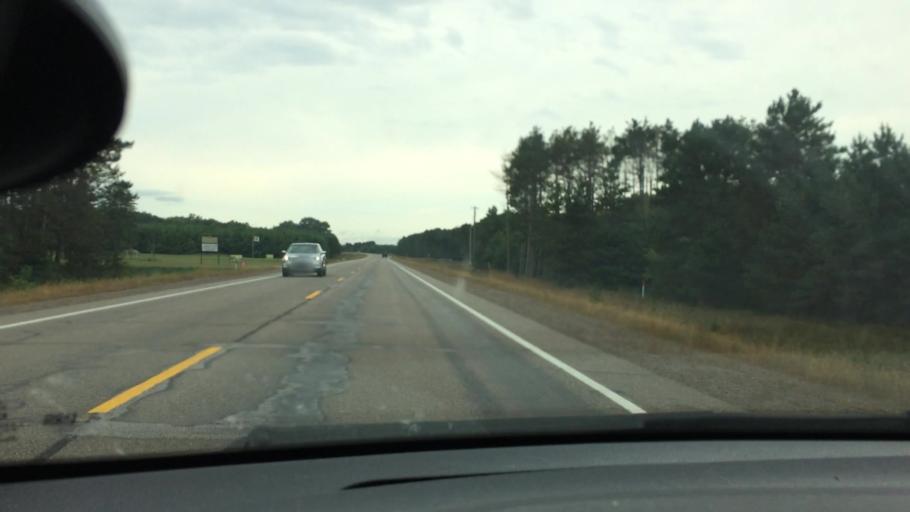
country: US
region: Wisconsin
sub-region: Eau Claire County
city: Augusta
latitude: 44.5827
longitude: -91.0886
